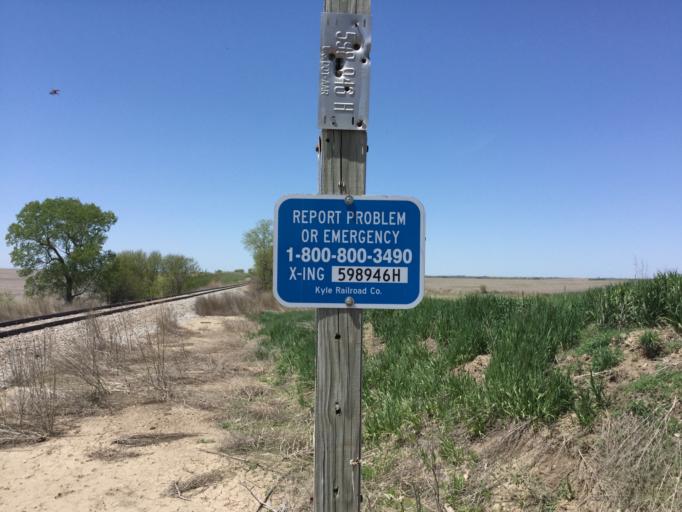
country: US
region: Kansas
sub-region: Smith County
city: Smith Center
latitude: 39.8067
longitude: -98.5793
